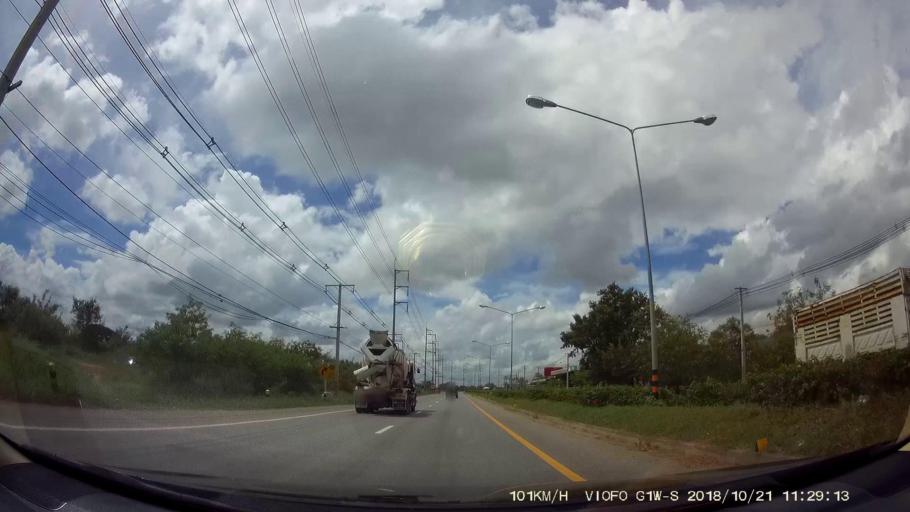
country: TH
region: Chaiyaphum
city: Chaiyaphum
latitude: 15.7865
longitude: 102.0337
